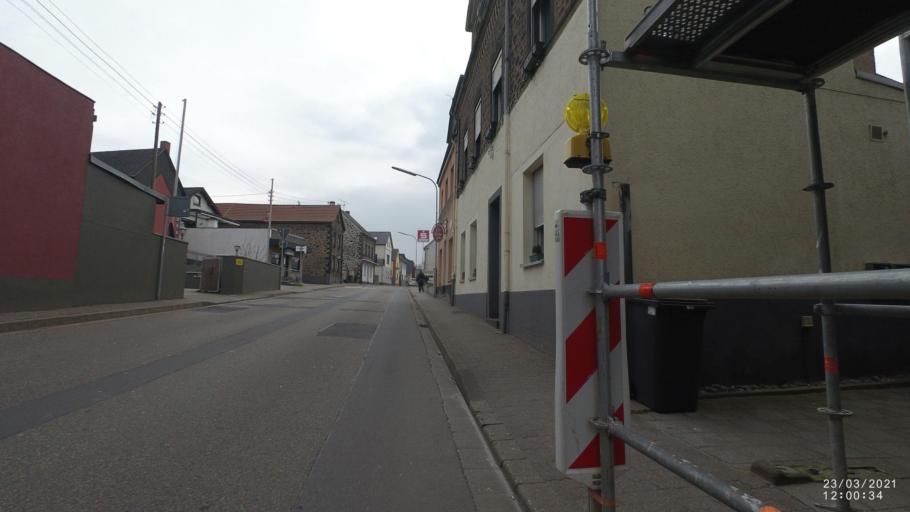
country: DE
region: Rheinland-Pfalz
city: Ochtendung
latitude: 50.3492
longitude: 7.3908
